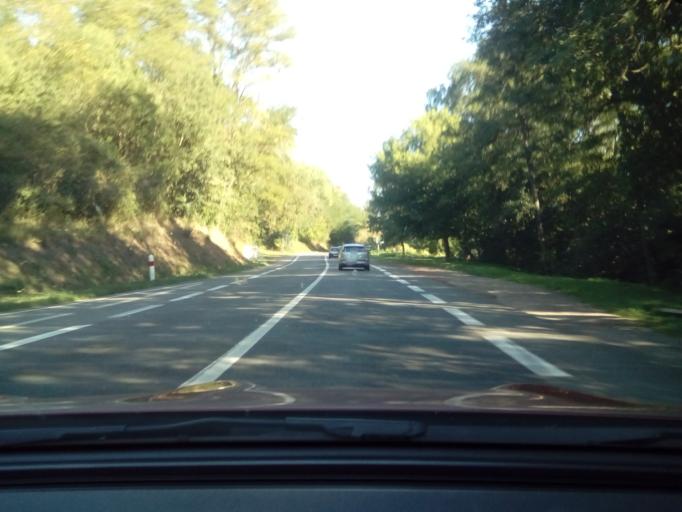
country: FR
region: Rhone-Alpes
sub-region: Departement du Rhone
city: Charnay
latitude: 45.8711
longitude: 4.6521
